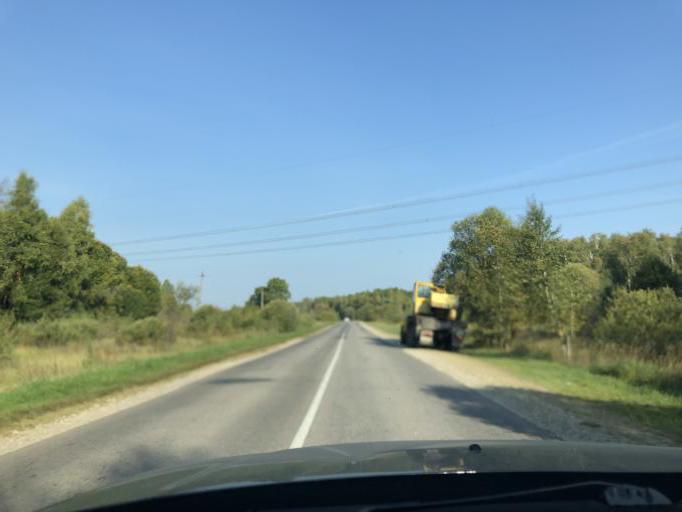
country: RU
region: Tula
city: Leninskiy
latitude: 54.3335
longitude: 37.3836
